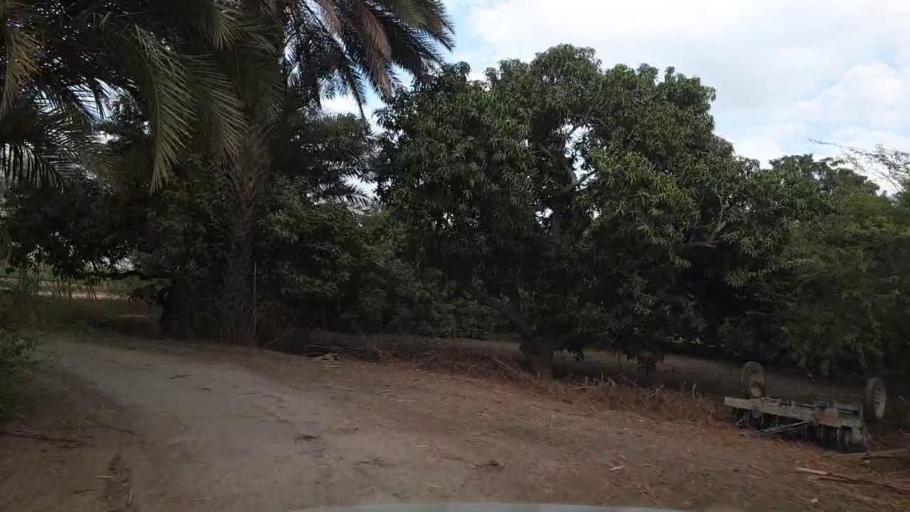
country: PK
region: Sindh
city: Tando Adam
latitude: 25.6543
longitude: 68.6085
